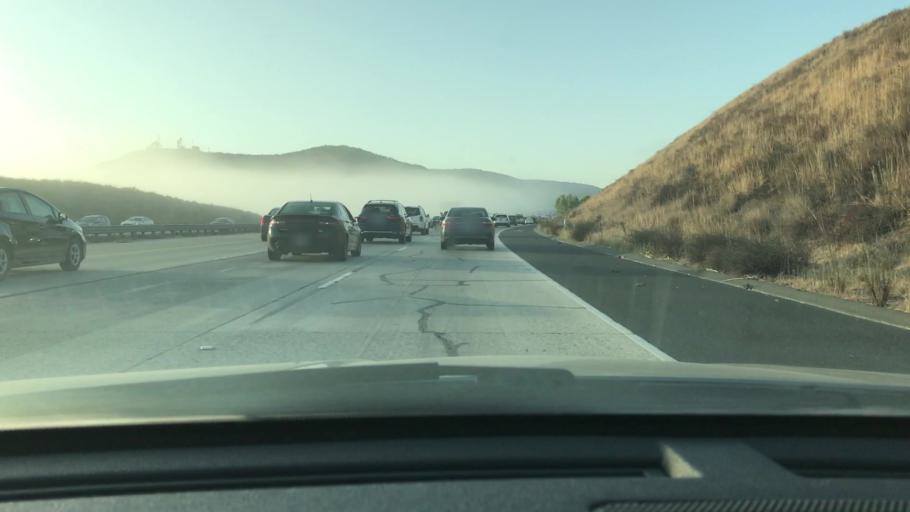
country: US
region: California
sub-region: Ventura County
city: Moorpark
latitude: 34.2548
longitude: -118.8405
